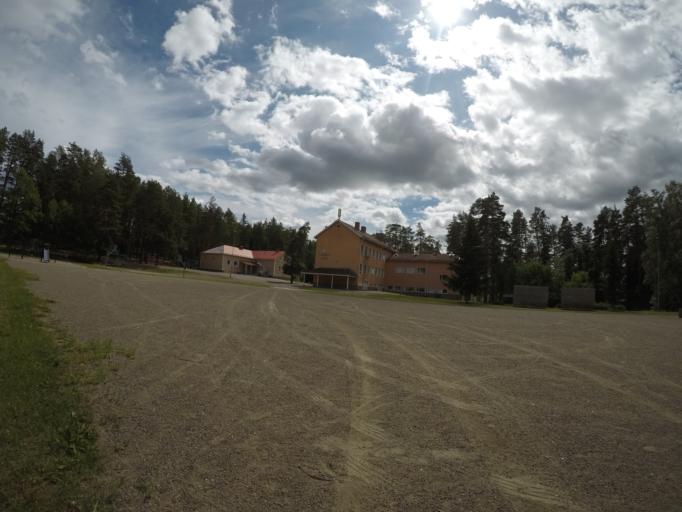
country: FI
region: Haeme
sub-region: Haemeenlinna
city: Haemeenlinna
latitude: 60.9735
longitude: 24.4250
